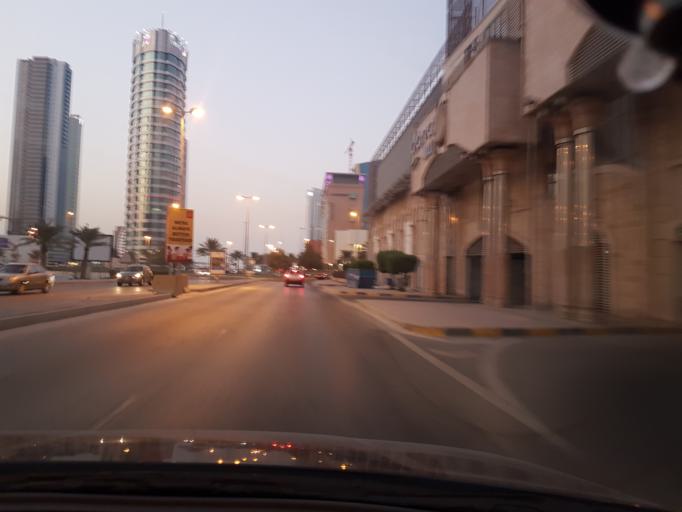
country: BH
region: Manama
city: Jidd Hafs
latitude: 26.2300
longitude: 50.5517
